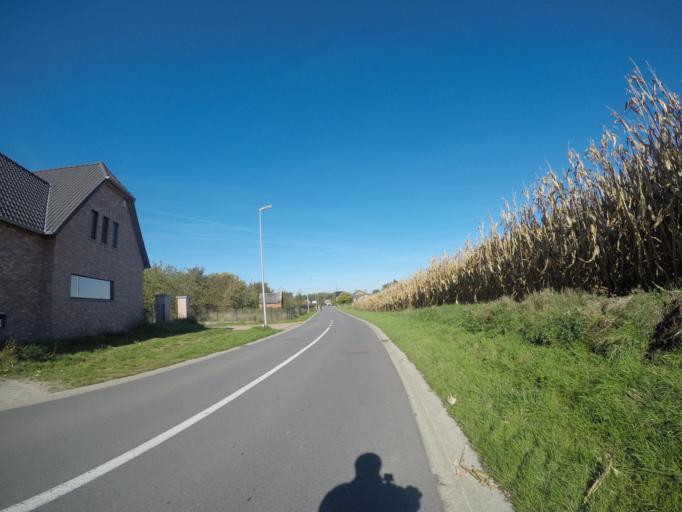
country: BE
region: Flanders
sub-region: Provincie Limburg
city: Alken
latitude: 50.8680
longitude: 5.2902
